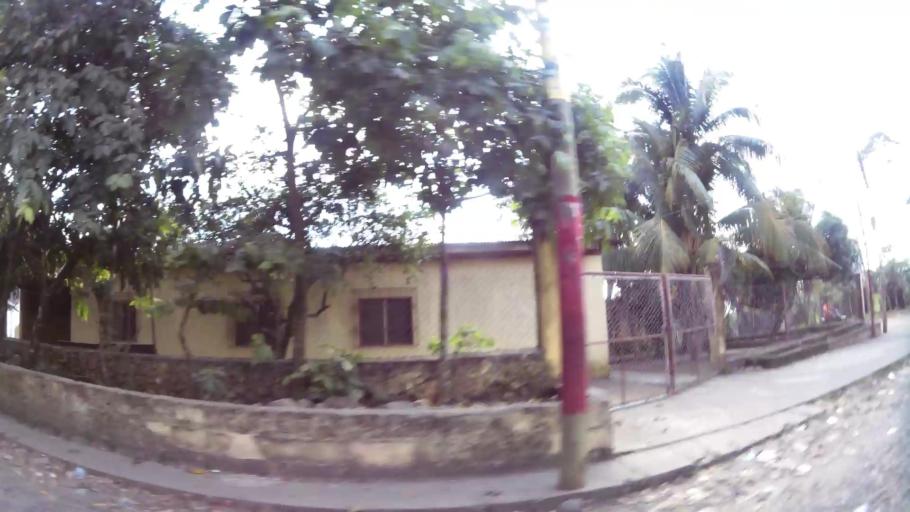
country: GT
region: Suchitepeque
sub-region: Municipio de Cuyotenango
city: Cuyotenango
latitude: 14.5452
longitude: -91.5710
